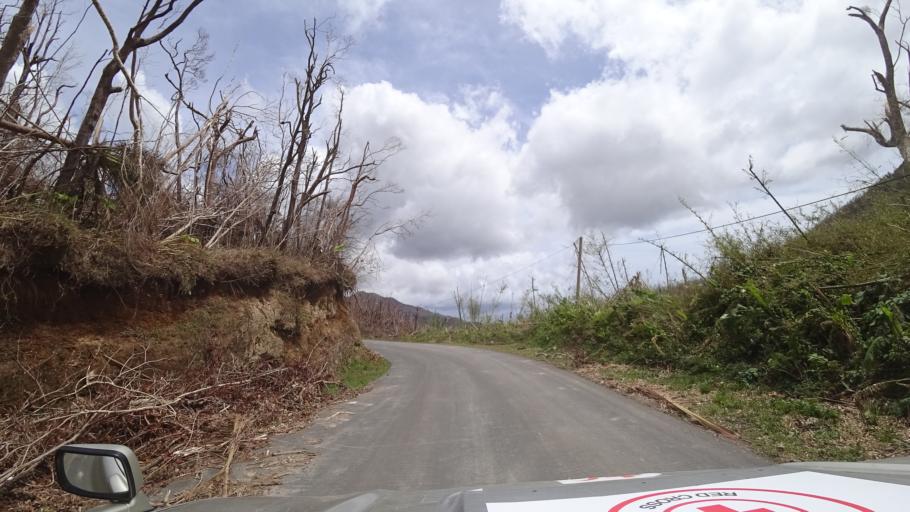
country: DM
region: Saint Luke
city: Pointe Michel
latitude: 15.2667
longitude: -61.3420
